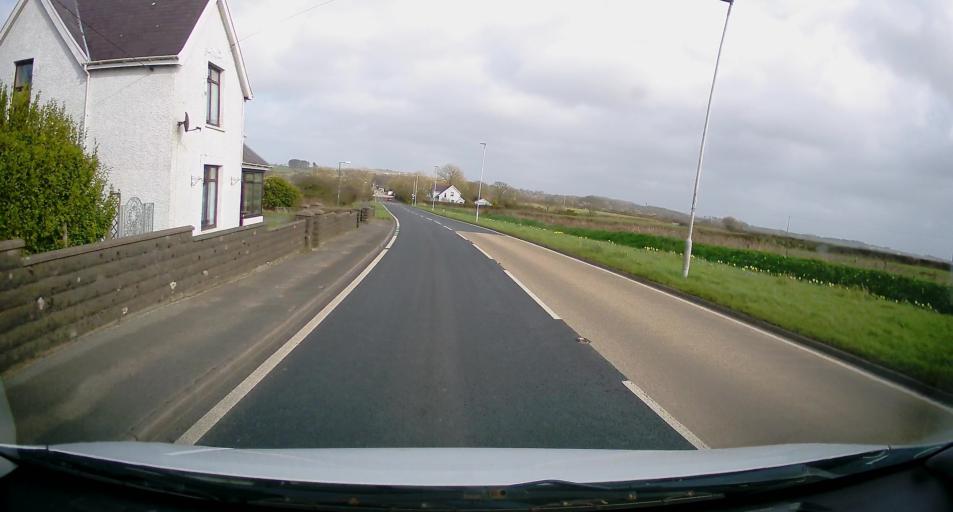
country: GB
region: Wales
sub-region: County of Ceredigion
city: Aberporth
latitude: 52.1094
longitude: -4.5365
